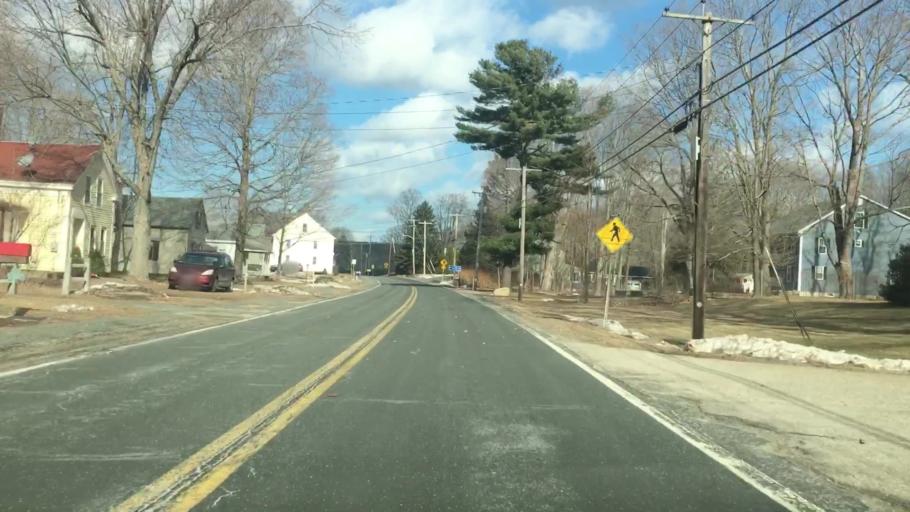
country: US
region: Massachusetts
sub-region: Hampden County
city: Wales
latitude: 42.0662
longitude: -72.2225
